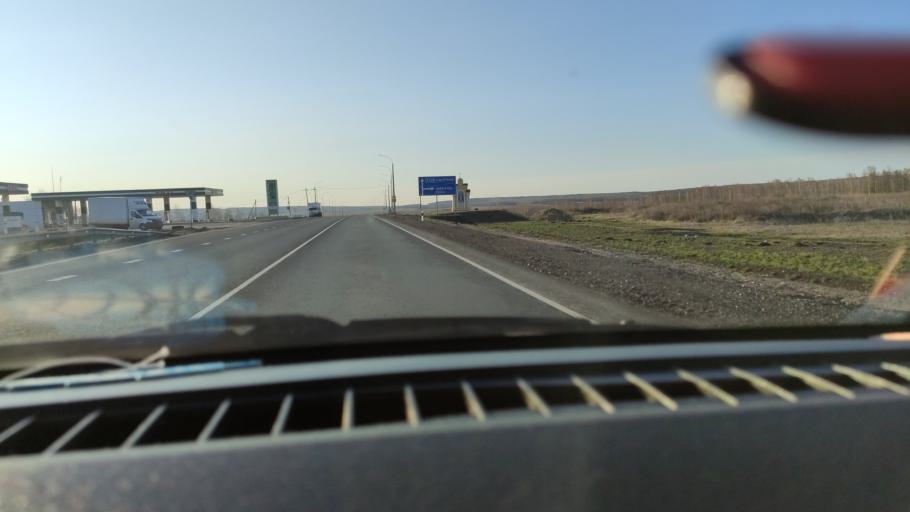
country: RU
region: Saratov
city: Shikhany
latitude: 52.1317
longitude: 47.2275
